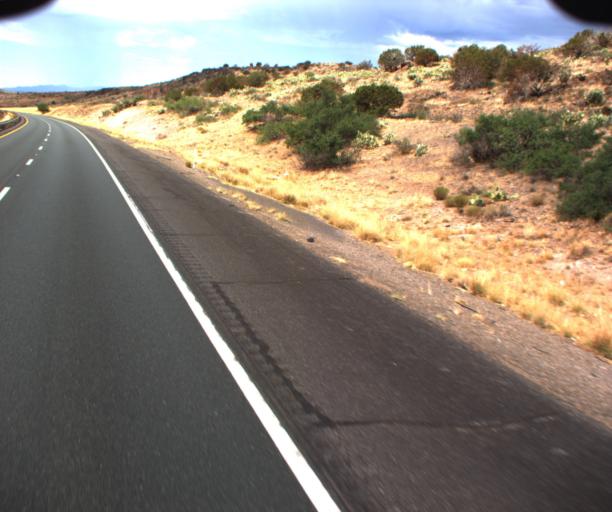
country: US
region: Arizona
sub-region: Yavapai County
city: Cordes Lakes
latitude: 34.4591
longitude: -112.0326
